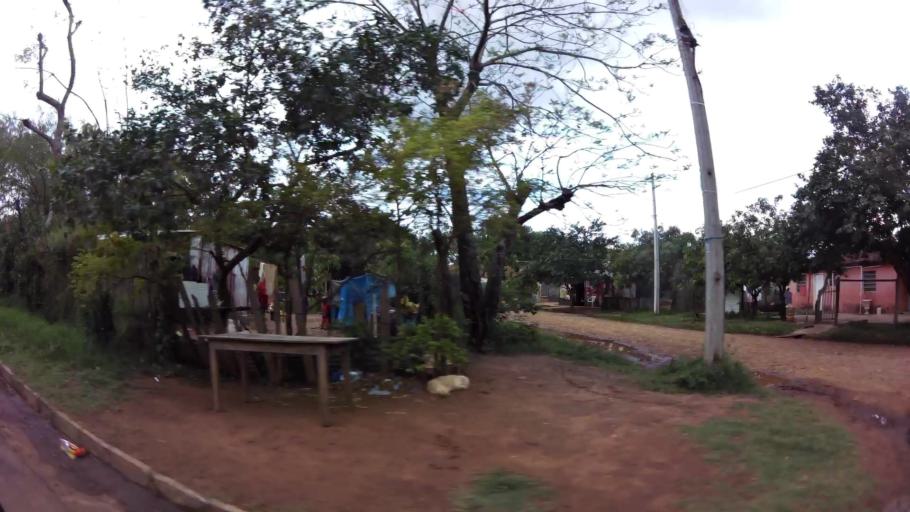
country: PY
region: Central
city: San Lorenzo
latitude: -25.2864
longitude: -57.4935
